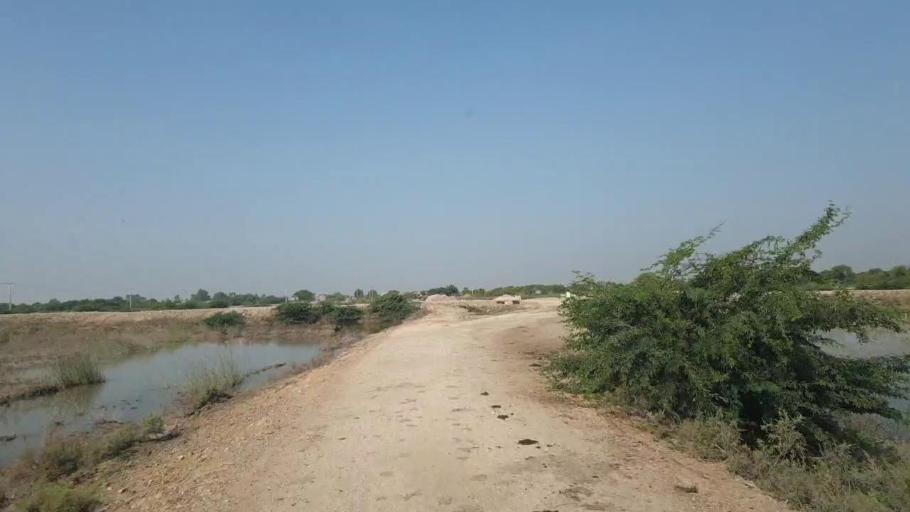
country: PK
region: Sindh
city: Badin
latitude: 24.5214
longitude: 68.7669
